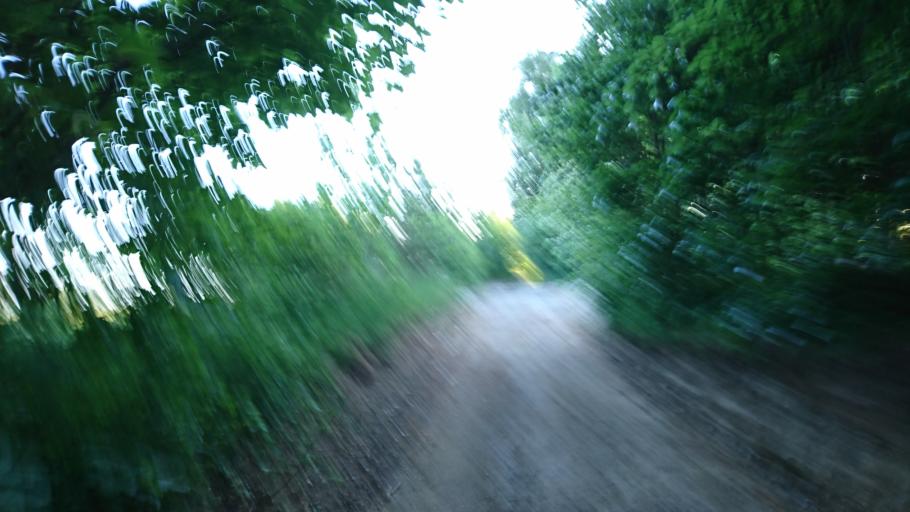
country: DK
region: Capital Region
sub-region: Ballerup Kommune
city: Malov
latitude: 55.7442
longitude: 12.3329
